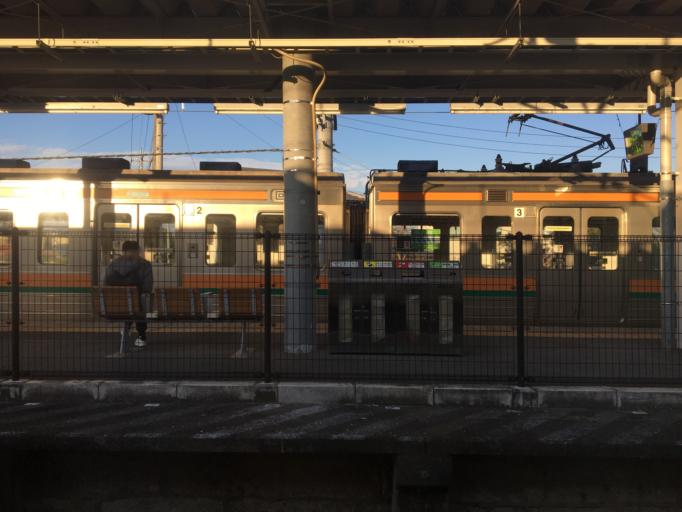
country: JP
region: Gunma
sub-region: Sawa-gun
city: Tamamura
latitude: 36.3543
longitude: 139.1393
